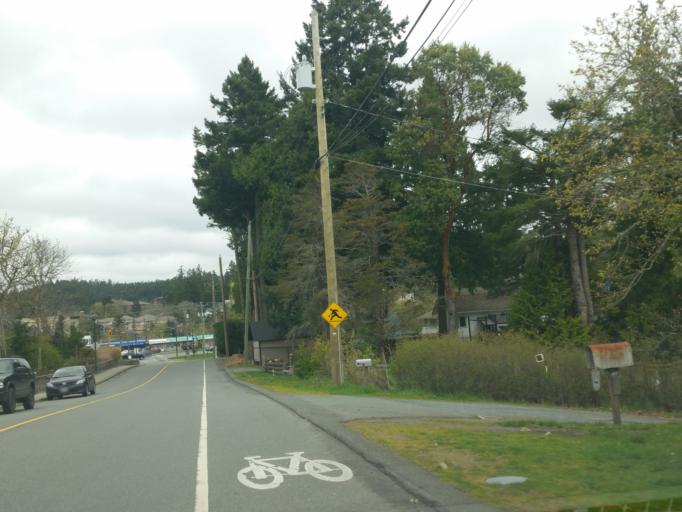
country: CA
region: British Columbia
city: Colwood
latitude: 48.4541
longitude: -123.4585
